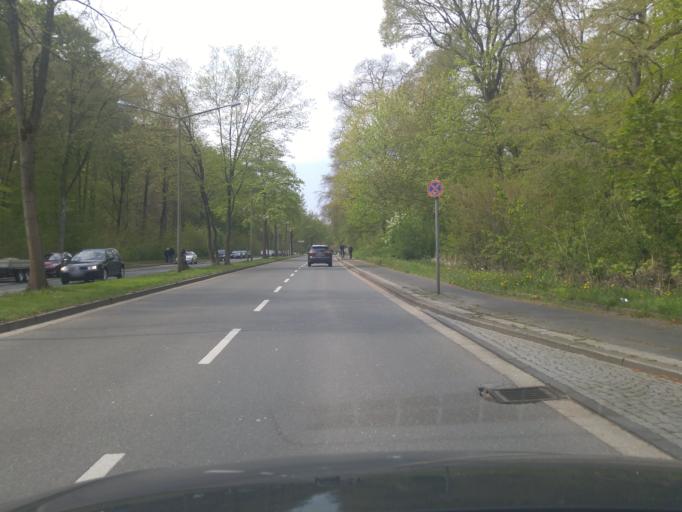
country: DE
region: North Rhine-Westphalia
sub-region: Regierungsbezirk Dusseldorf
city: Essen
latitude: 51.4189
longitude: 7.0148
